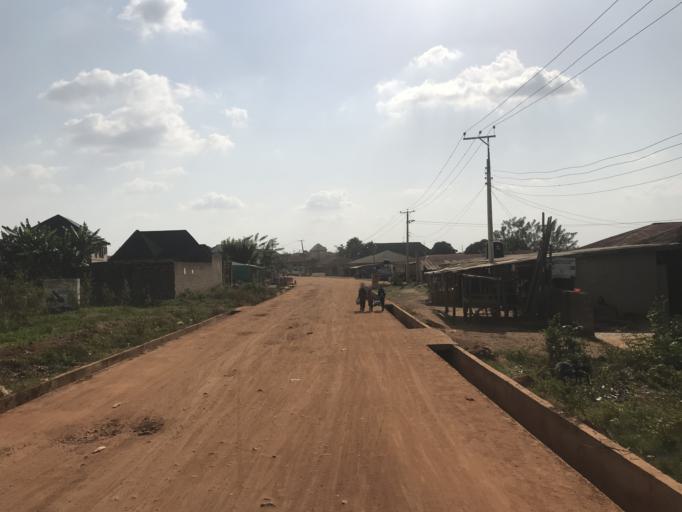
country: NG
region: Osun
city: Osogbo
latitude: 7.8112
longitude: 4.5592
